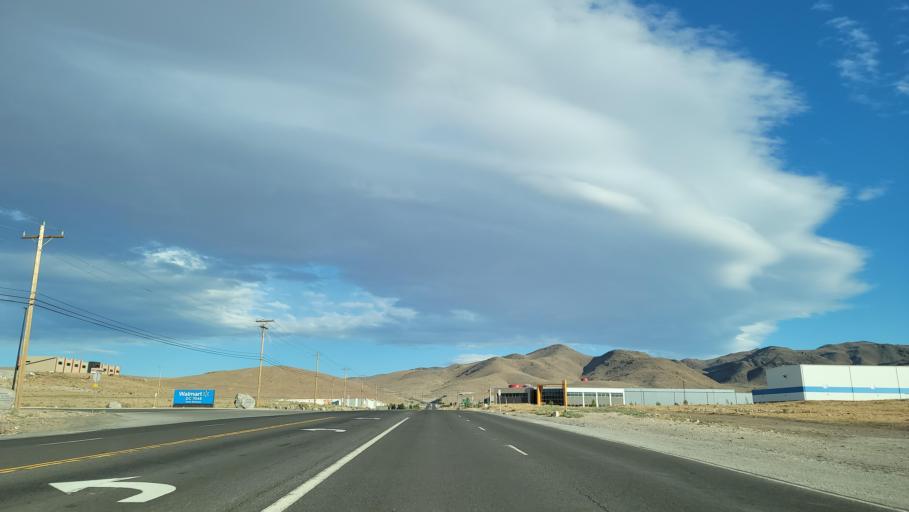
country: US
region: Nevada
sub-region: Lyon County
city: Stagecoach
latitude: 39.5342
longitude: -119.4842
